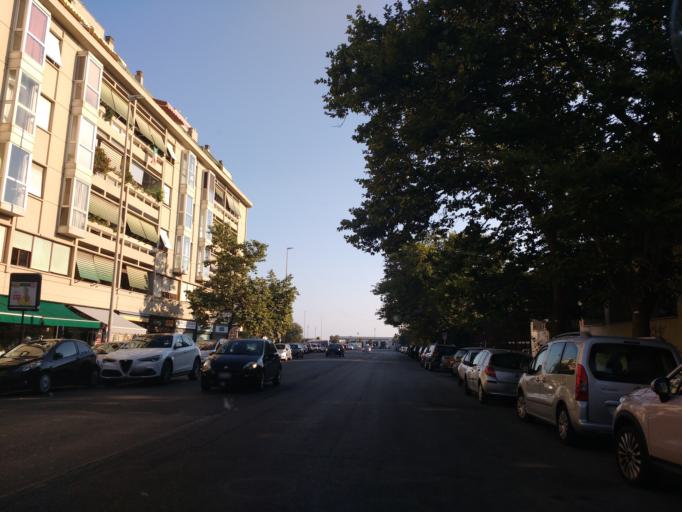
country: IT
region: Latium
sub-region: Citta metropolitana di Roma Capitale
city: Lido di Ostia
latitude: 41.7330
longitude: 12.2736
